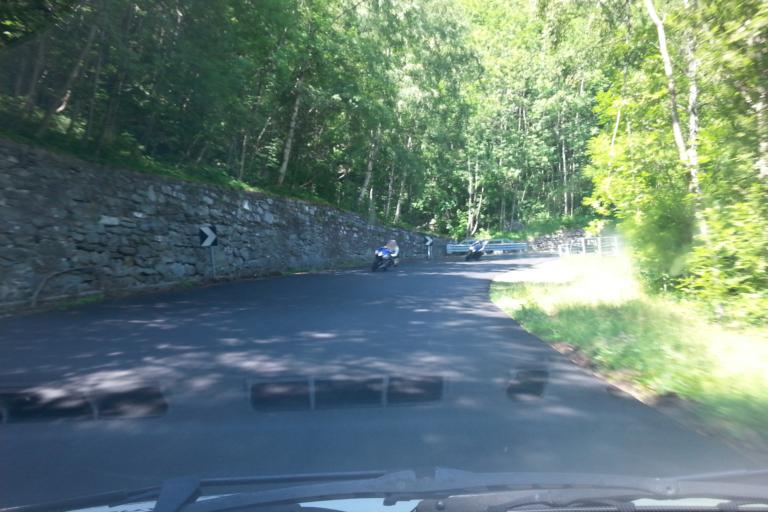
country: IT
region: Piedmont
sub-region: Provincia di Torino
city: Moncenisio
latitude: 45.1828
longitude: 6.9884
